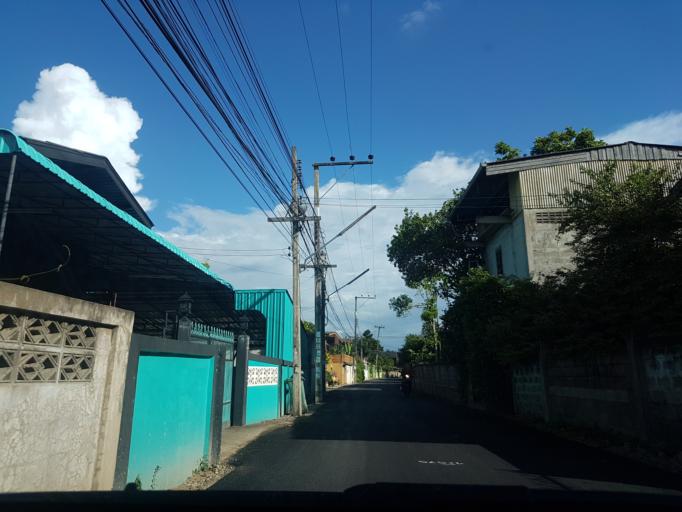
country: TH
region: Lampang
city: Ko Kha
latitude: 18.2334
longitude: 99.4209
